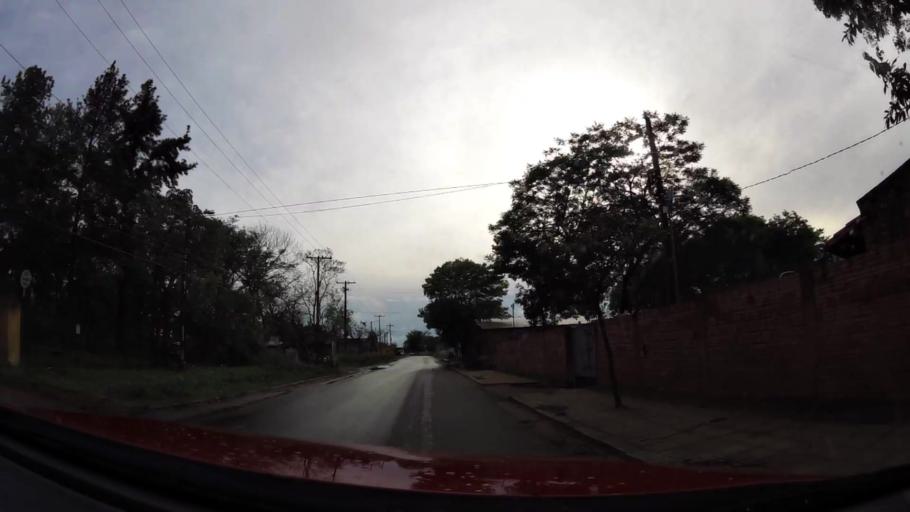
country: PY
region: Central
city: Limpio
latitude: -25.2090
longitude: -57.5087
